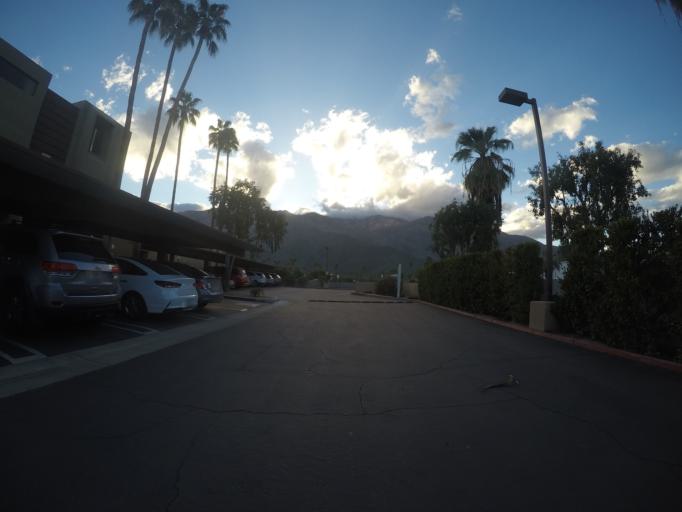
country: US
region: California
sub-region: Riverside County
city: Palm Springs
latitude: 33.8012
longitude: -116.5300
